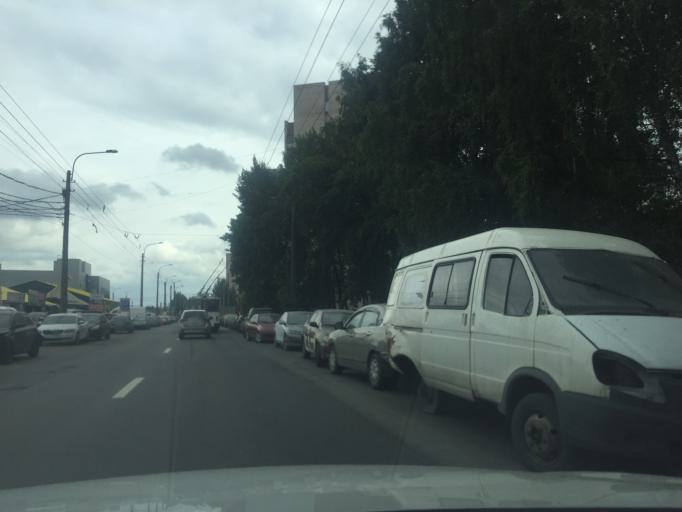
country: RU
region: Leningrad
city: Parnas
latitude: 60.0566
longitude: 30.3553
